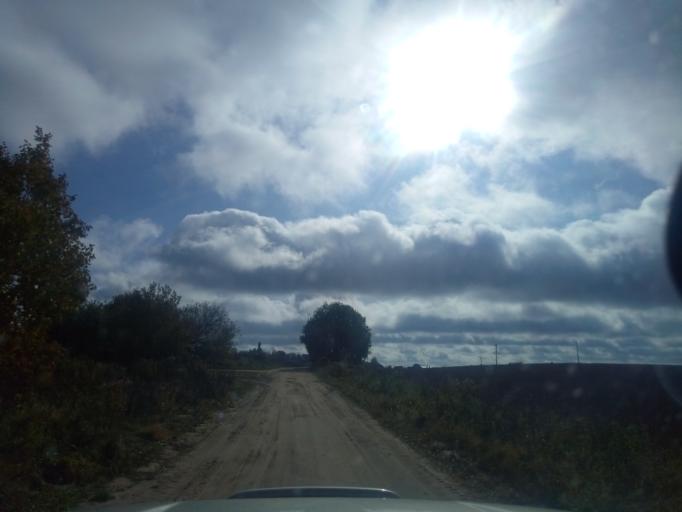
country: BY
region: Minsk
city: Zaslawye
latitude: 54.0216
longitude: 27.2886
